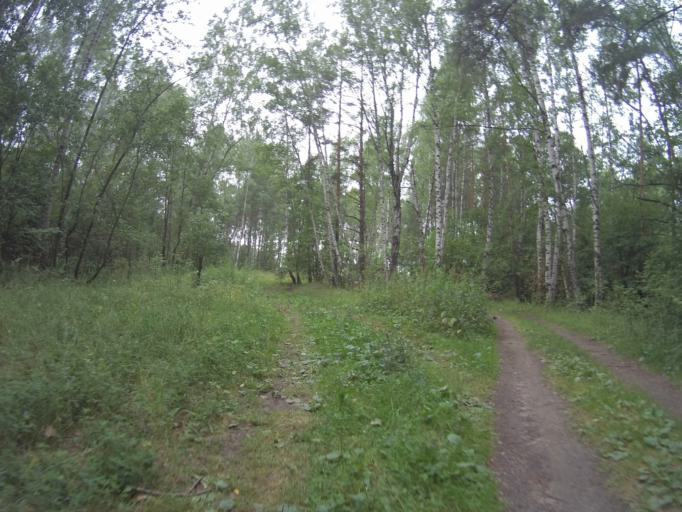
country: RU
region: Vladimir
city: Raduzhnyy
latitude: 55.9911
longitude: 40.2181
